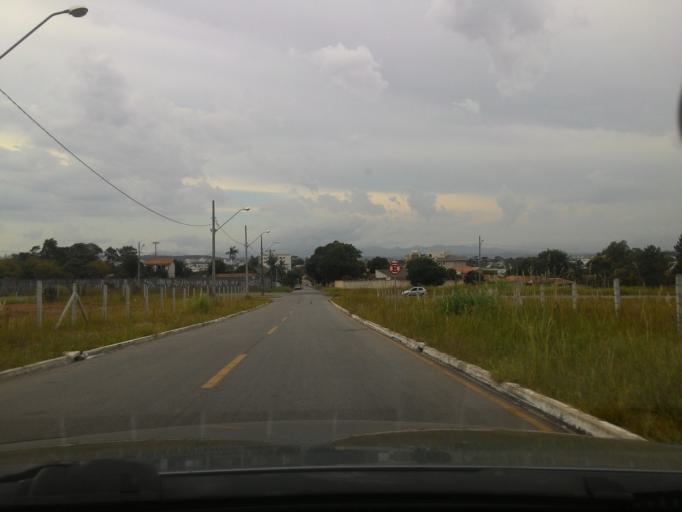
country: BR
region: Parana
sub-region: Pinhais
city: Pinhais
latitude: -25.4363
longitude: -49.1842
